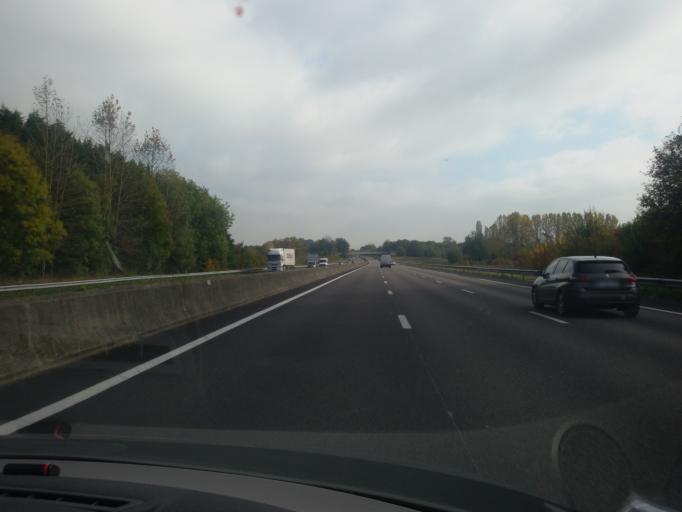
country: FR
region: Haute-Normandie
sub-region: Departement de l'Eure
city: Saint-Ouen-de-Thouberville
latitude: 49.3563
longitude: 0.8780
